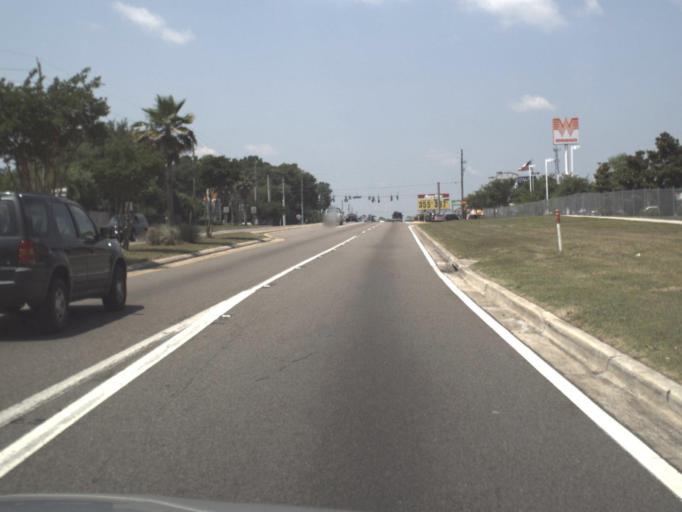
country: US
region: Florida
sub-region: Clay County
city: Bellair-Meadowbrook Terrace
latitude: 30.2961
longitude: -81.7742
